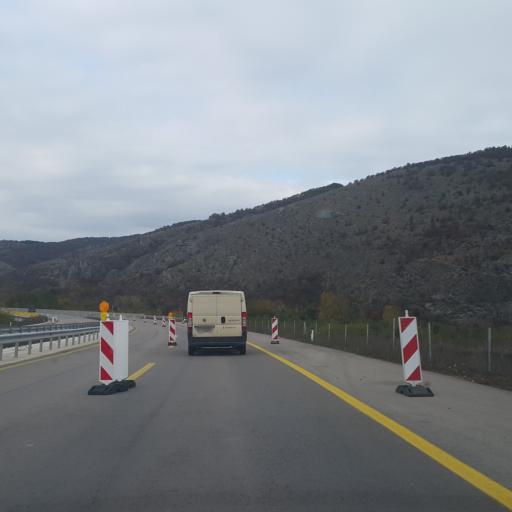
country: RS
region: Central Serbia
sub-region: Pirotski Okrug
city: Bela Palanka
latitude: 43.2324
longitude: 22.3788
